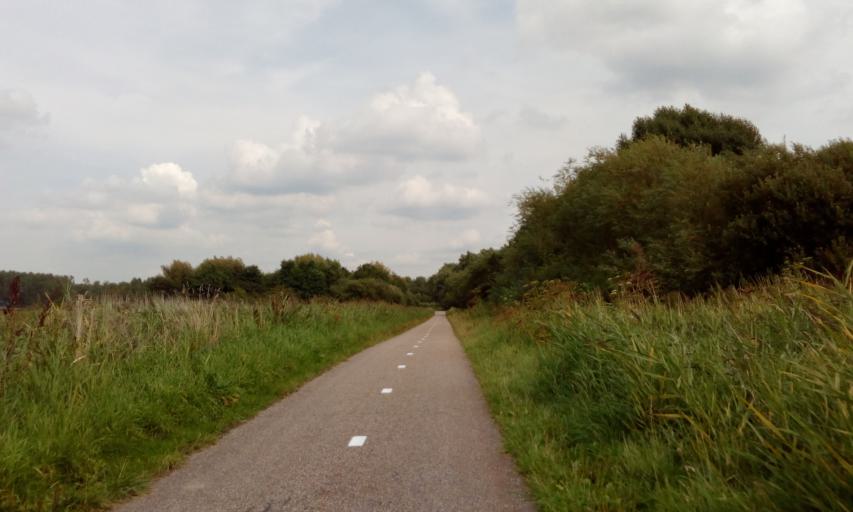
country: NL
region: South Holland
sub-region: Gemeente Pijnacker-Nootdorp
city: Pijnacker
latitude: 52.0362
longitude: 4.4413
